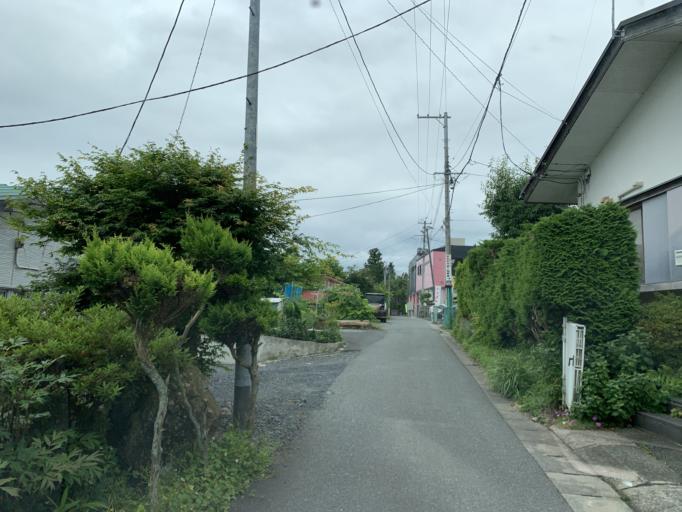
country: JP
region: Iwate
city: Ichinoseki
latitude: 38.9213
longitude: 141.1319
